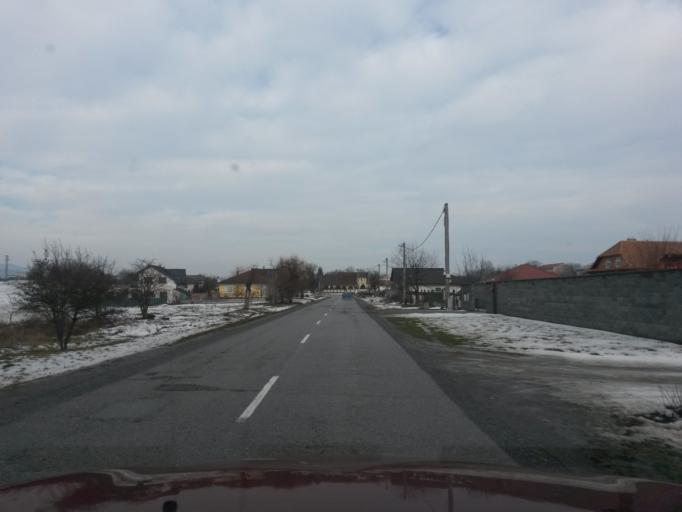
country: SK
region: Kosicky
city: Kosice
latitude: 48.7794
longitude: 21.3302
